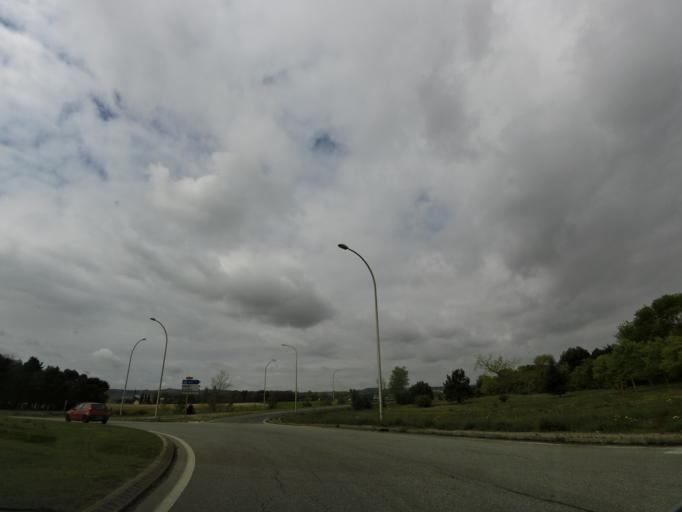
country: FR
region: Languedoc-Roussillon
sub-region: Departement de l'Aude
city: Castelnaudary
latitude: 43.3004
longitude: 1.9675
